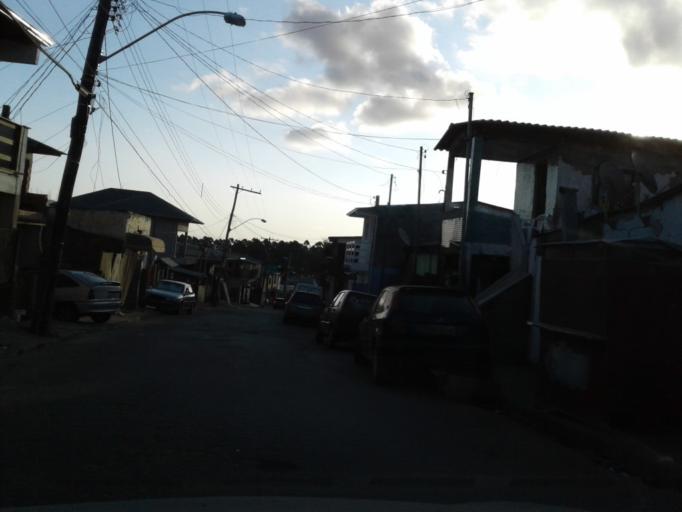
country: BR
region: Rio Grande do Sul
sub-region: Porto Alegre
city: Porto Alegre
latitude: -30.0494
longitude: -51.1512
